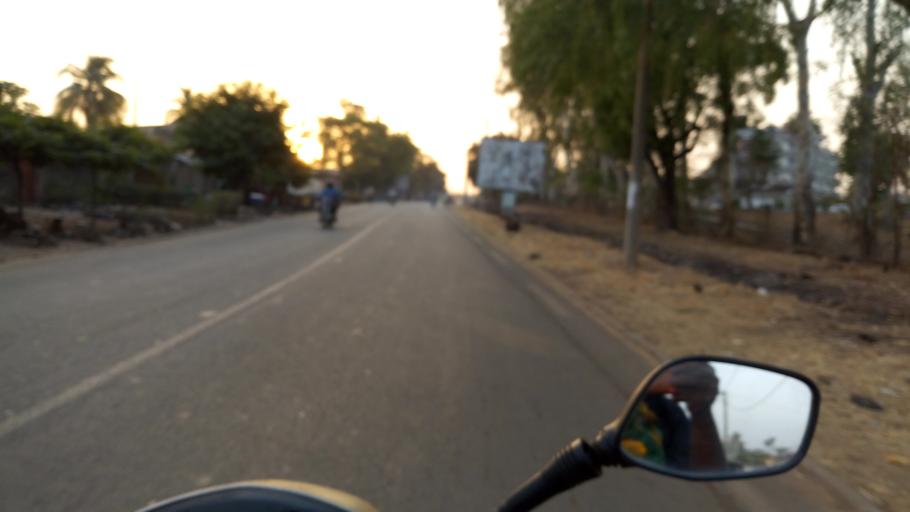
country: TG
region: Kara
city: Kara
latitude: 9.5496
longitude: 1.1841
